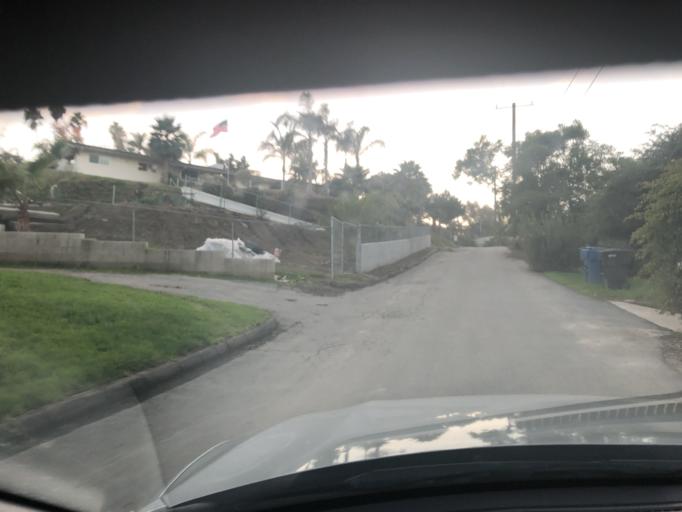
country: US
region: California
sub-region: San Diego County
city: Chula Vista
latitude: 32.6438
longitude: -117.0593
